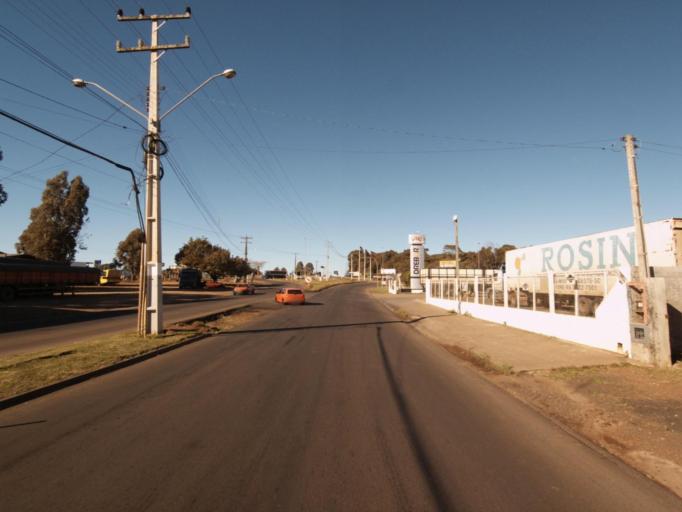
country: AR
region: Misiones
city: Bernardo de Irigoyen
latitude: -26.7598
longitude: -53.5005
